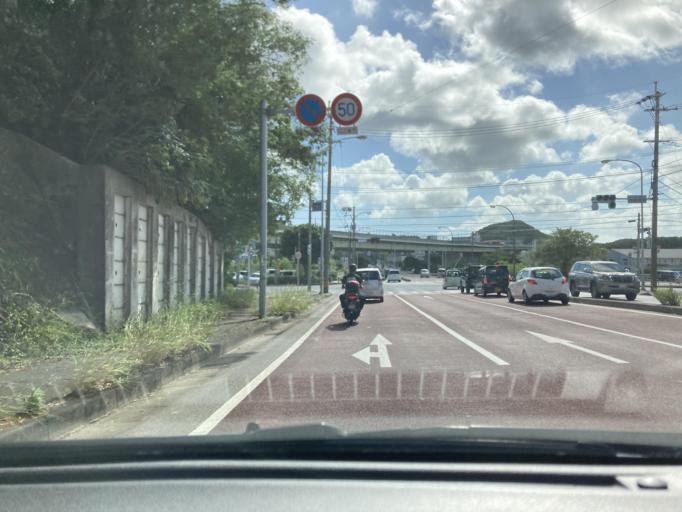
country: JP
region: Okinawa
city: Tomigusuku
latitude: 26.1809
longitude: 127.7167
